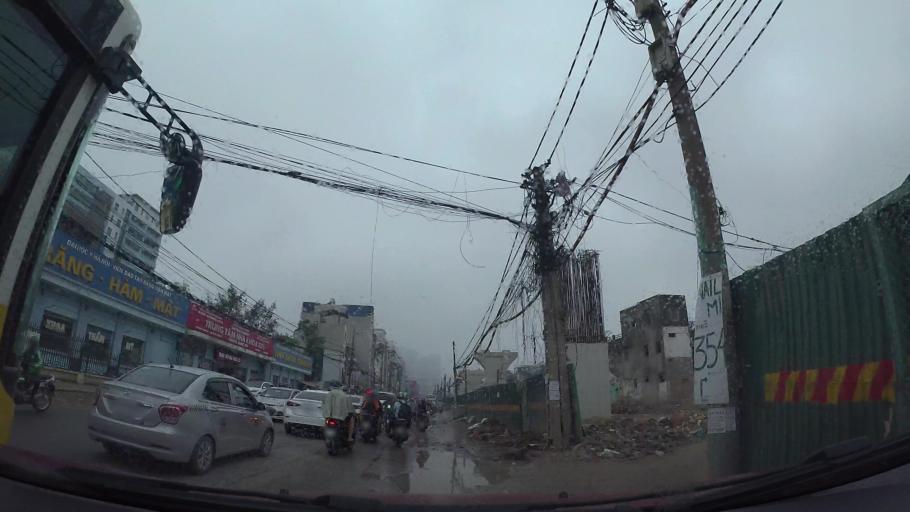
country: VN
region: Ha Noi
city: Dong Da
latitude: 21.0015
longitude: 105.8262
